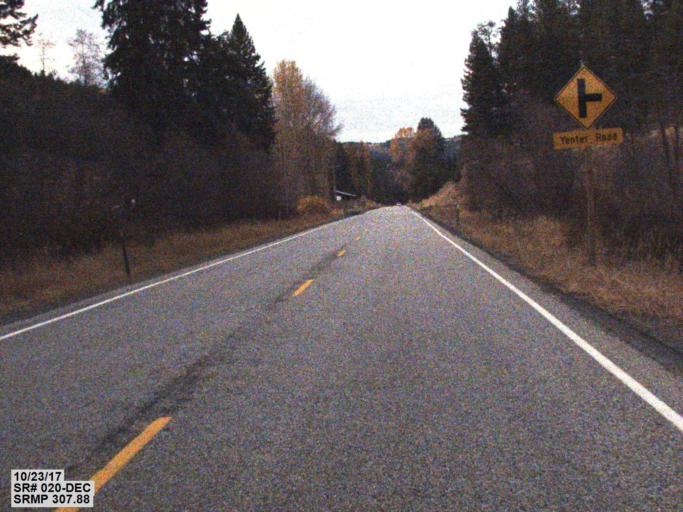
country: US
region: Washington
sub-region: Ferry County
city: Republic
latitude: 48.6161
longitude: -118.6665
